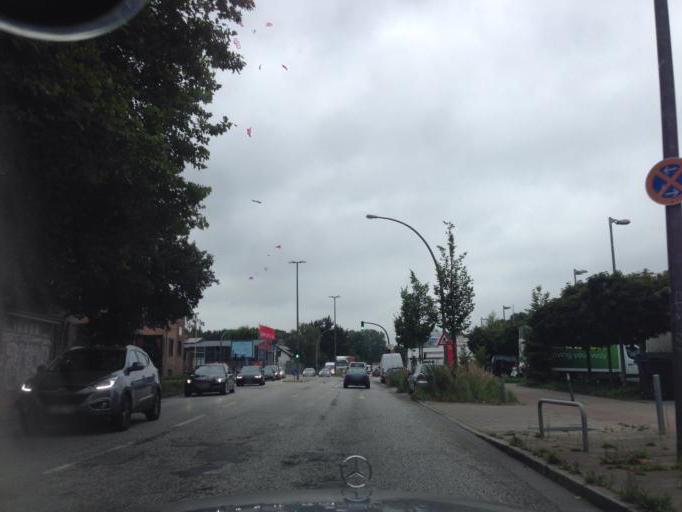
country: DE
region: Hamburg
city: Altona
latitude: 53.5668
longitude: 9.9184
